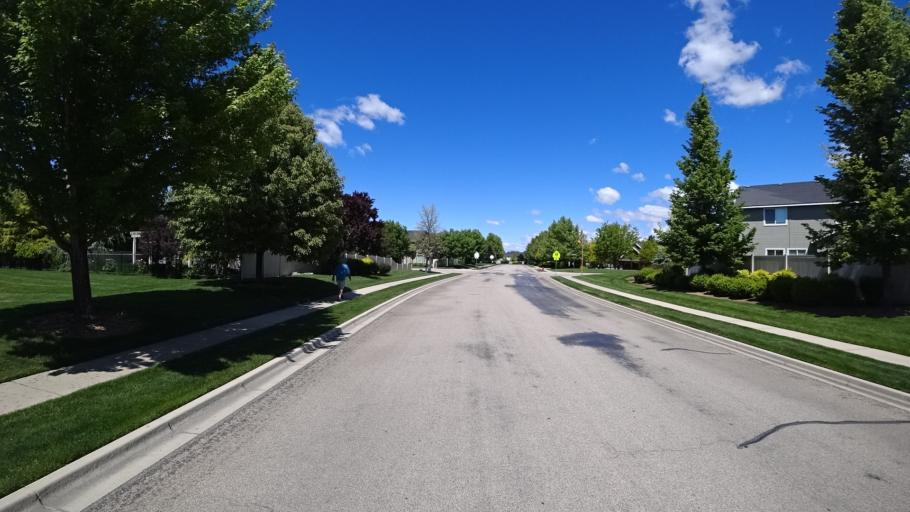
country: US
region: Idaho
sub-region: Ada County
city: Meridian
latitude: 43.6297
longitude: -116.3412
